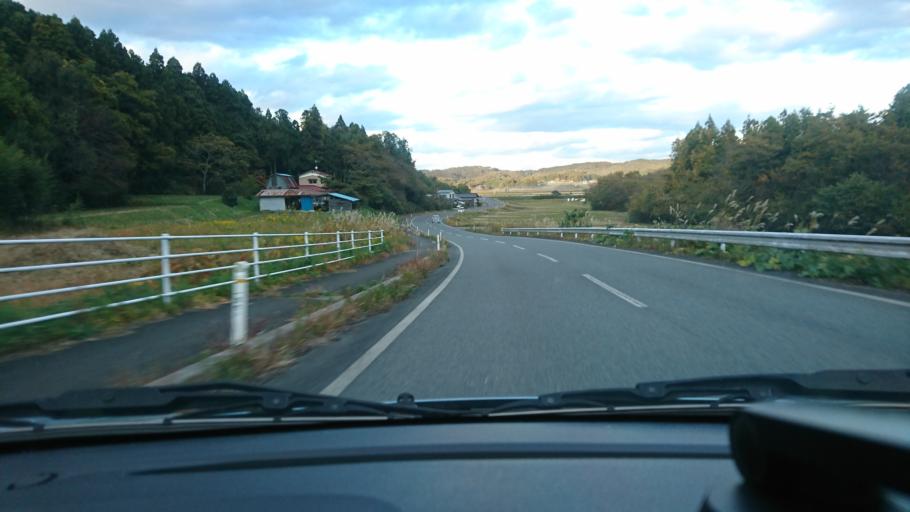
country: JP
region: Iwate
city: Ichinoseki
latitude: 38.8094
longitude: 141.1957
